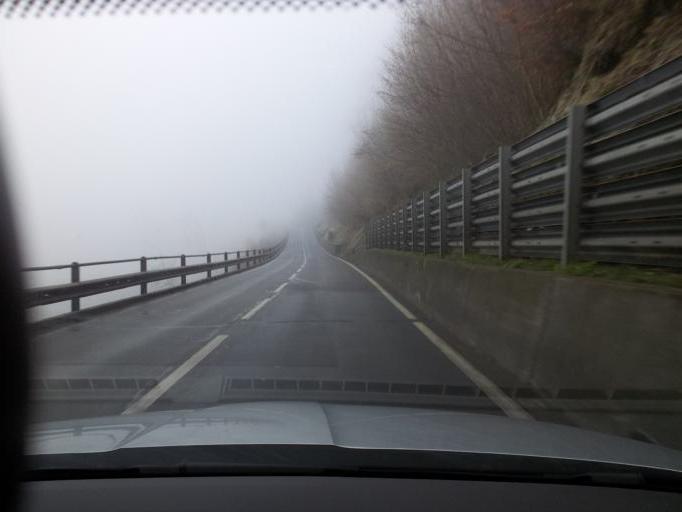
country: CH
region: Lucerne
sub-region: Lucerne-Stadt District
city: Littau
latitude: 47.0392
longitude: 8.2401
